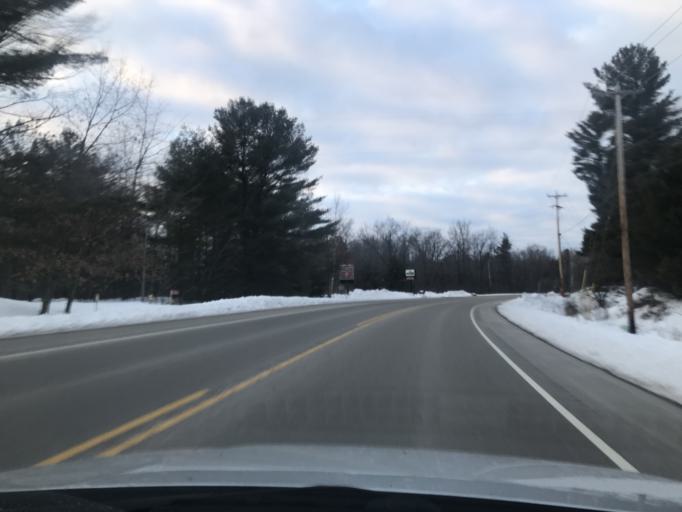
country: US
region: Wisconsin
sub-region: Marinette County
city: Marinette
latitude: 45.1158
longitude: -87.6798
